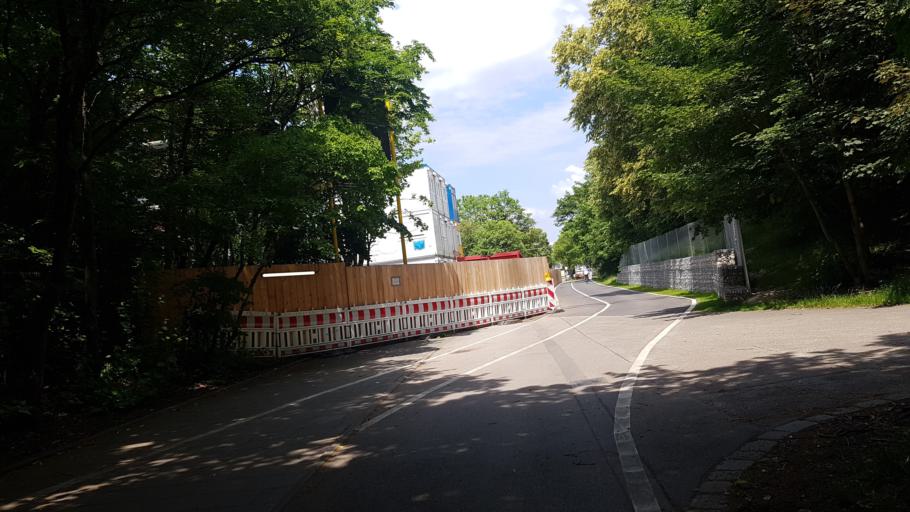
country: DE
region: Bavaria
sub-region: Upper Bavaria
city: Neuried
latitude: 48.1219
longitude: 11.5073
